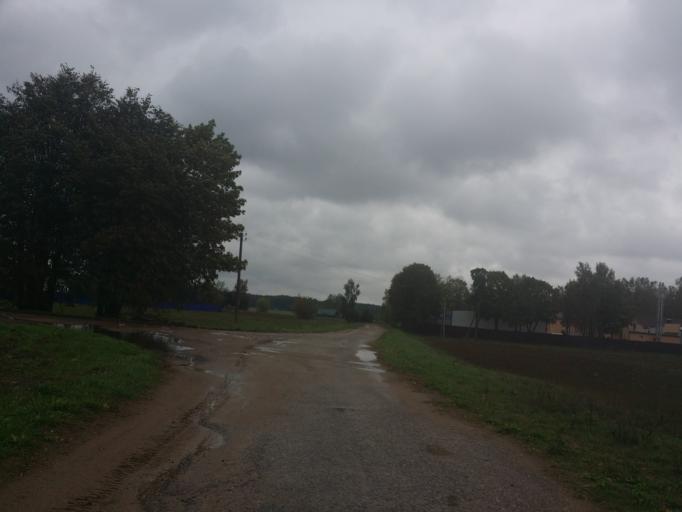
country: BY
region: Minsk
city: Chervyen'
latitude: 53.7648
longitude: 28.2517
